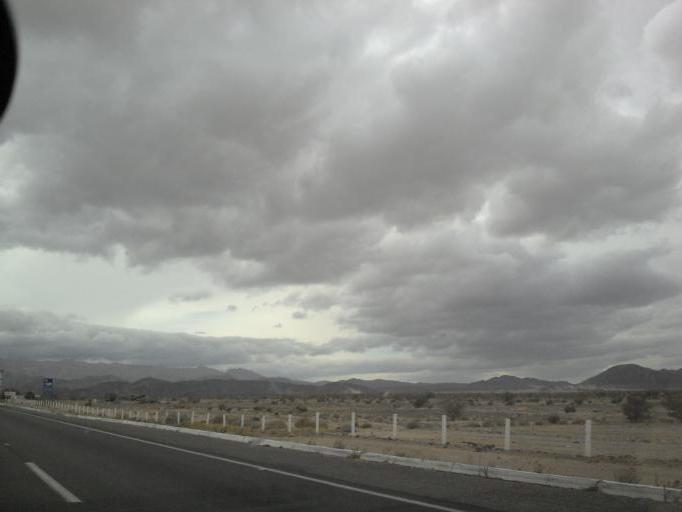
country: US
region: California
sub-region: Imperial County
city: Seeley
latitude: 32.5650
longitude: -115.8852
